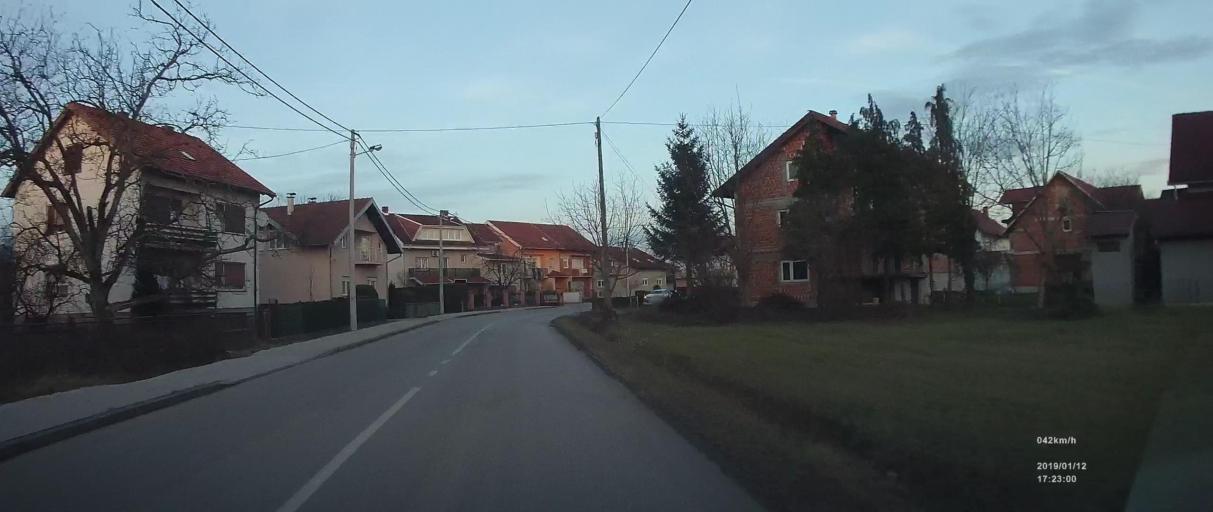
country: HR
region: Zagrebacka
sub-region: Grad Velika Gorica
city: Velika Gorica
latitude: 45.7270
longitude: 16.0890
